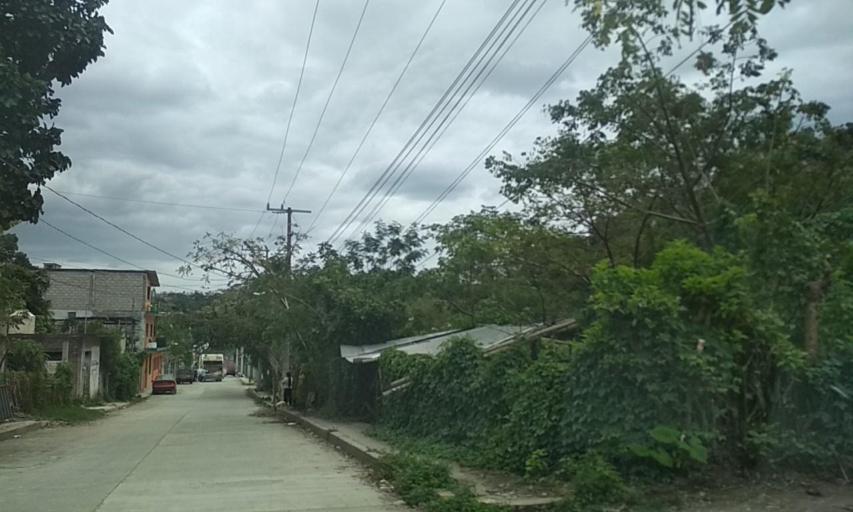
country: MX
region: Veracruz
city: Papantla de Olarte
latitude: 20.4596
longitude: -97.3145
